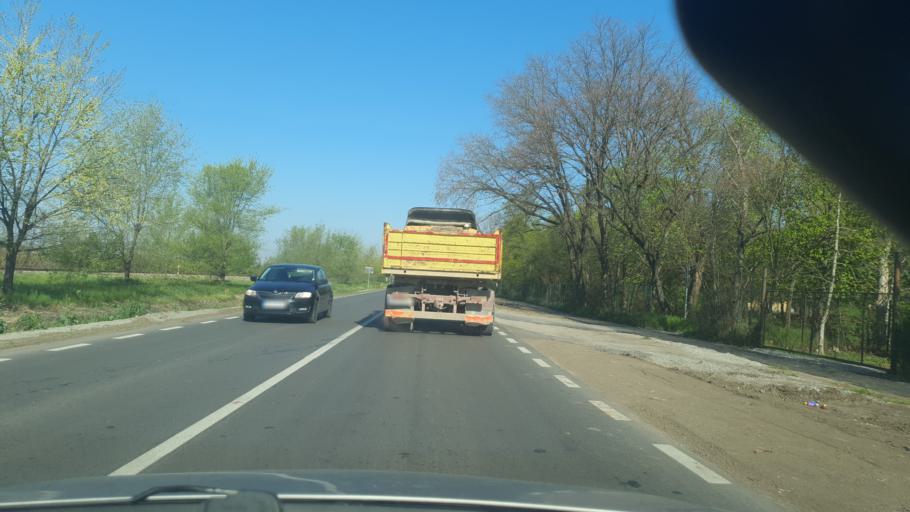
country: RS
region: Autonomna Pokrajina Vojvodina
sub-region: Juznobacki Okrug
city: Vrbas
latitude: 45.5893
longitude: 19.5971
